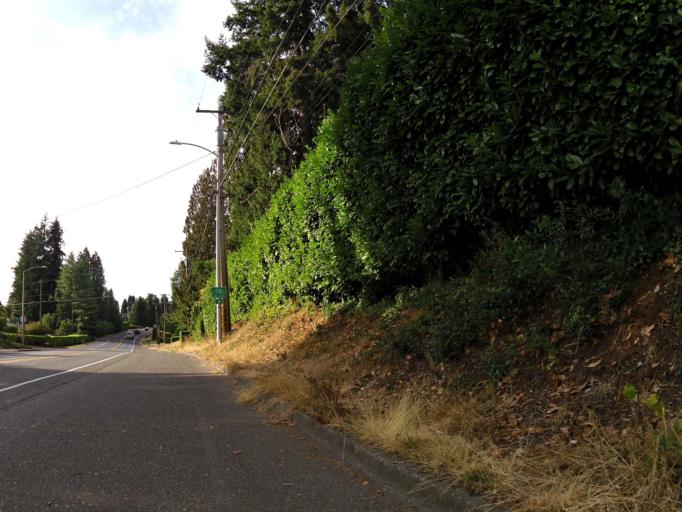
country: US
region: Washington
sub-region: Cowlitz County
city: Longview Heights
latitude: 46.1649
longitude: -122.9641
